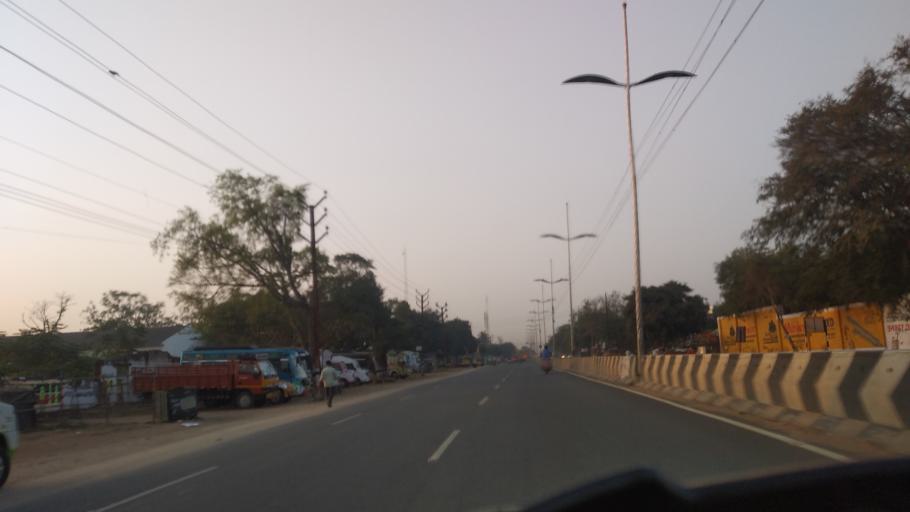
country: IN
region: Tamil Nadu
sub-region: Coimbatore
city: Madukkarai
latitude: 10.9470
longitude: 76.9533
